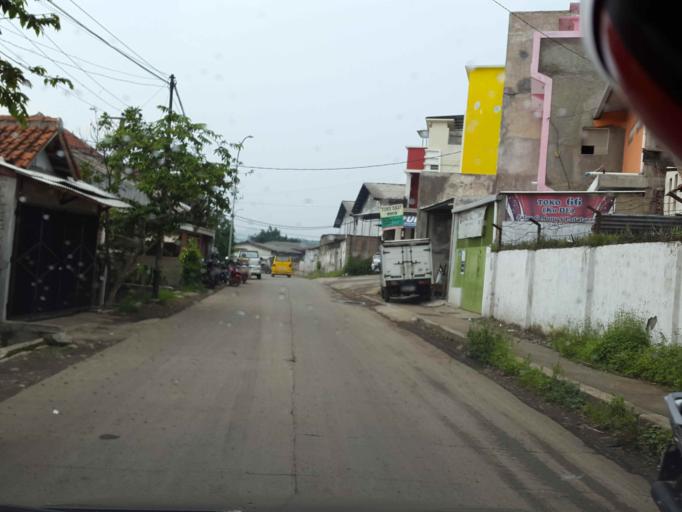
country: ID
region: West Java
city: Padalarang
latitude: -6.8427
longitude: 107.4961
